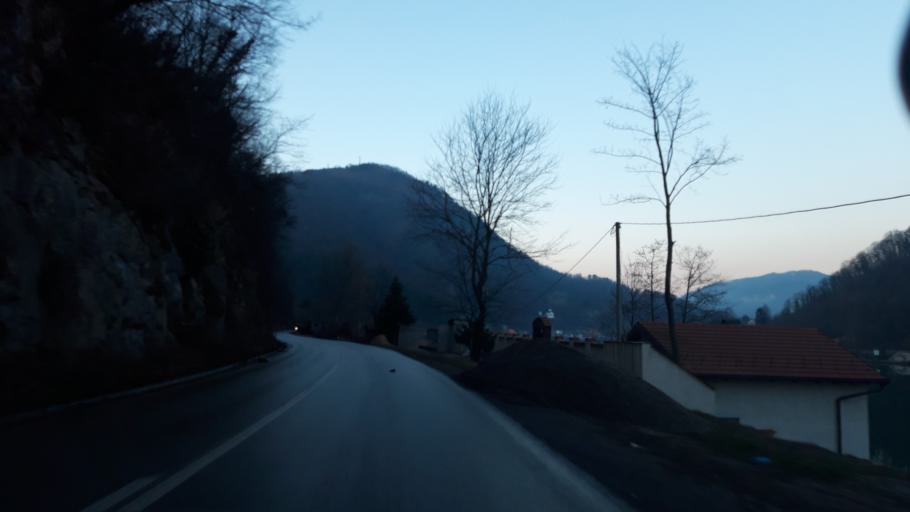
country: RS
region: Central Serbia
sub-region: Macvanski Okrug
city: Mali Zvornik
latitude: 44.3496
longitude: 19.1102
